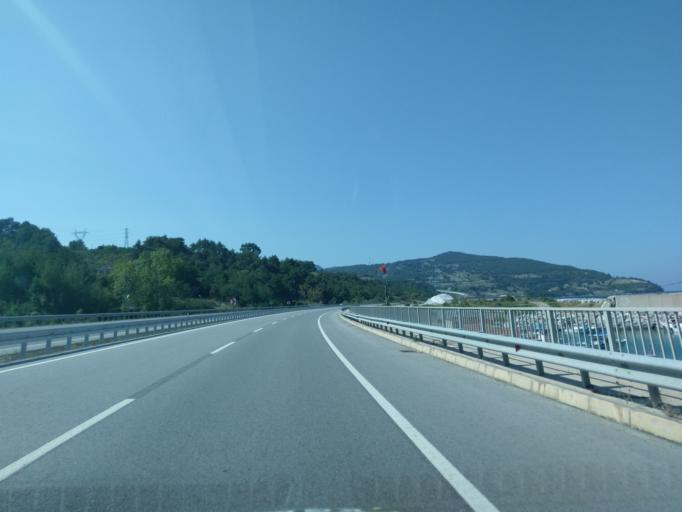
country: TR
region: Sinop
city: Dikmen
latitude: 41.7154
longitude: 35.2773
